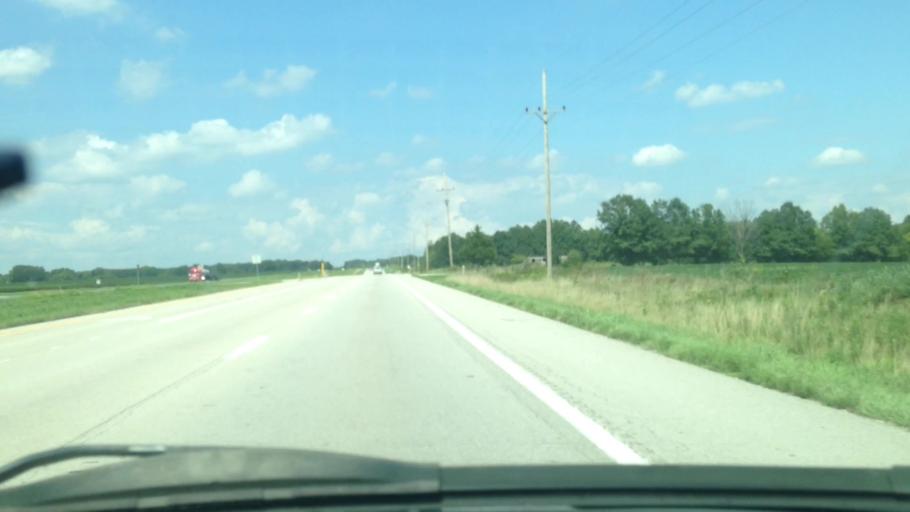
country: US
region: Missouri
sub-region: Lincoln County
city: Troy
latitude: 39.0970
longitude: -90.9658
